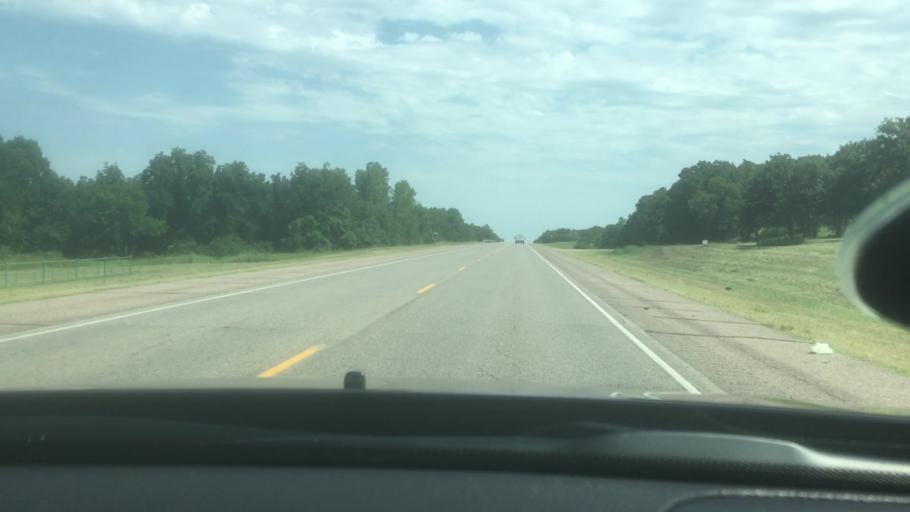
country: US
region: Oklahoma
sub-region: Seminole County
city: Konawa
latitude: 35.0053
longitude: -96.9314
